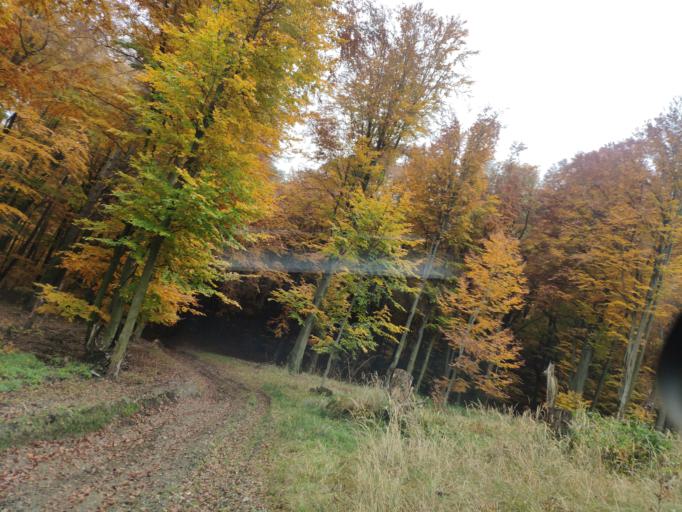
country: SK
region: Kosicky
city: Moldava nad Bodvou
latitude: 48.7313
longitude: 21.0195
